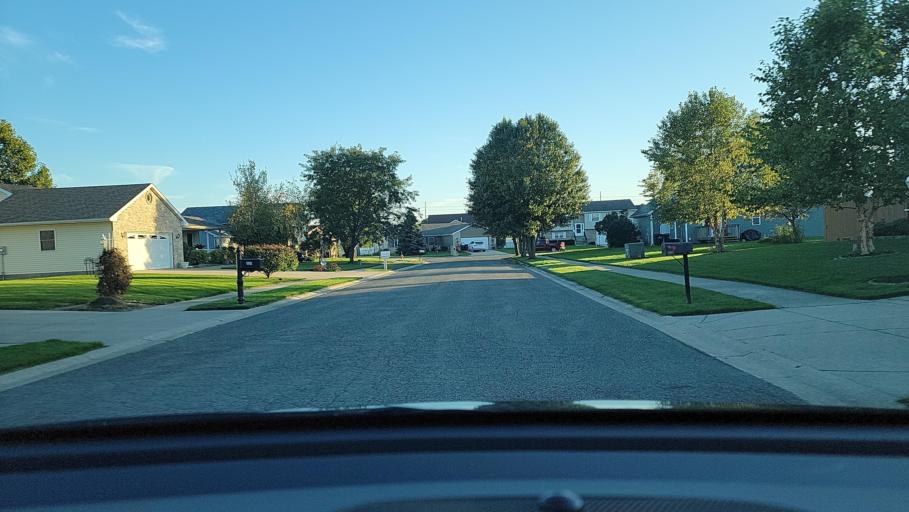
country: US
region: Indiana
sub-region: Porter County
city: Portage
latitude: 41.5384
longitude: -87.1927
